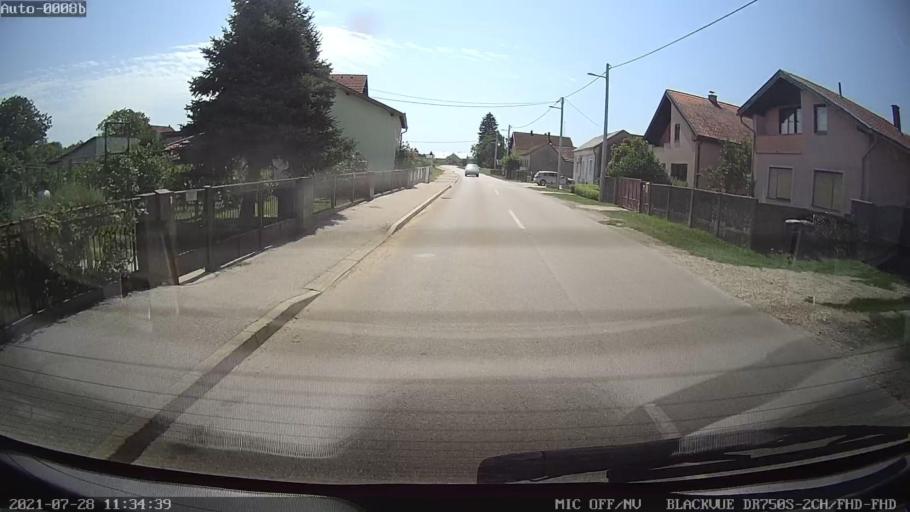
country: HR
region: Varazdinska
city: Varazdin
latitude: 46.2919
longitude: 16.3752
